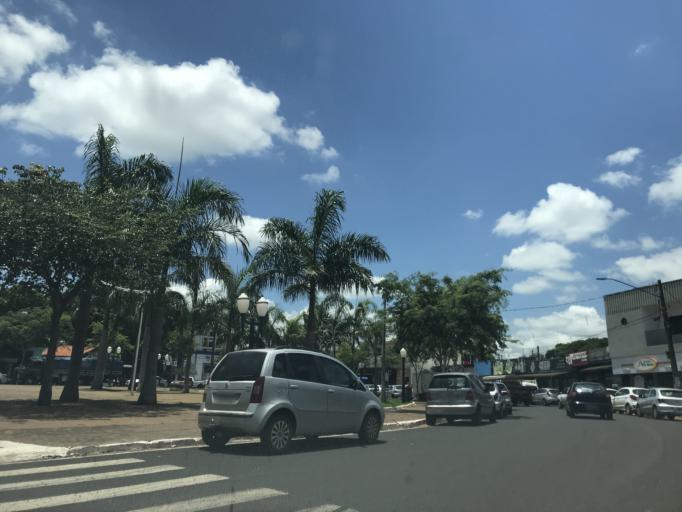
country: BR
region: Parana
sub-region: Marialva
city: Marialva
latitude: -23.4858
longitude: -51.7981
